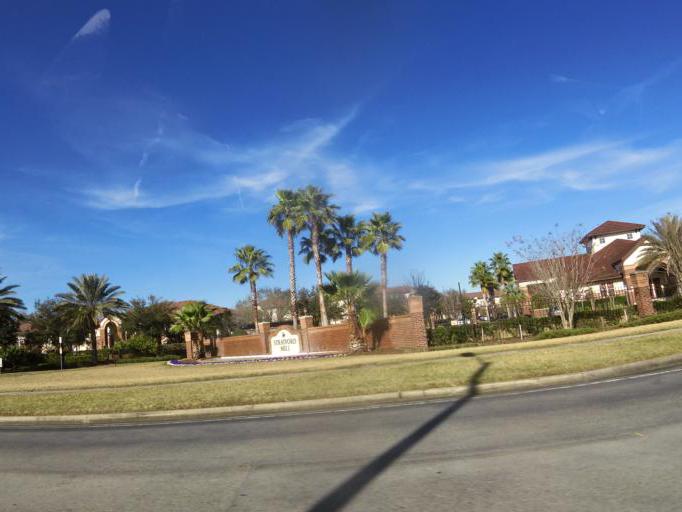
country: US
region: Florida
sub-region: Saint Johns County
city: Saint Augustine
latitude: 29.9252
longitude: -81.4089
